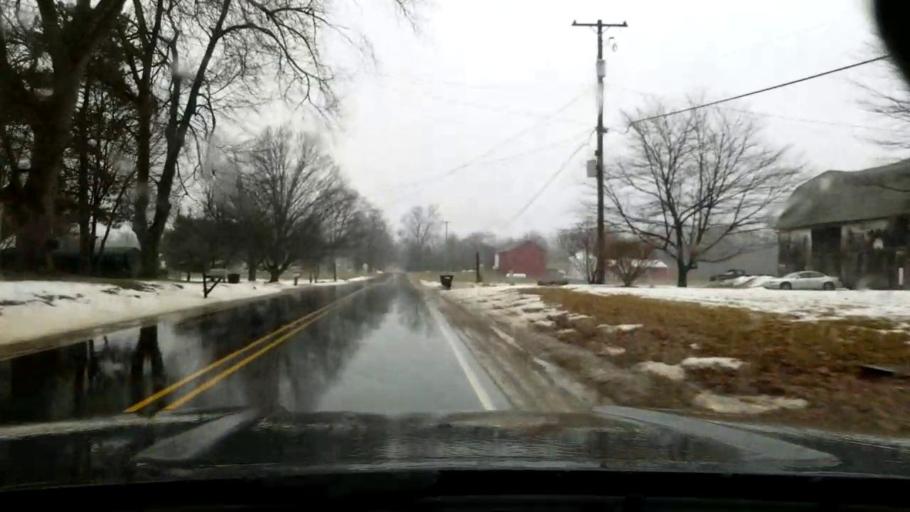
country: US
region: Michigan
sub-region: Jackson County
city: Michigan Center
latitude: 42.3072
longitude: -84.3093
